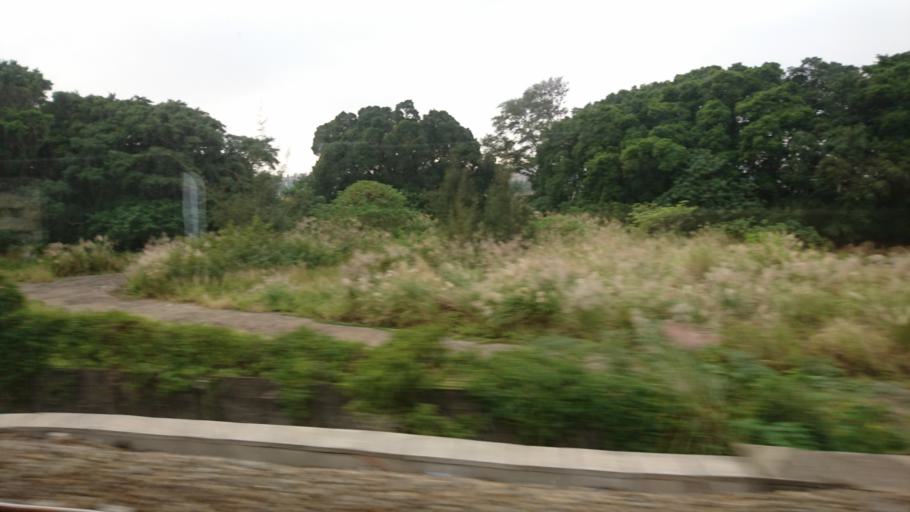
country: TW
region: Taiwan
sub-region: Hsinchu
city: Zhubei
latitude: 24.8454
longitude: 121.0135
